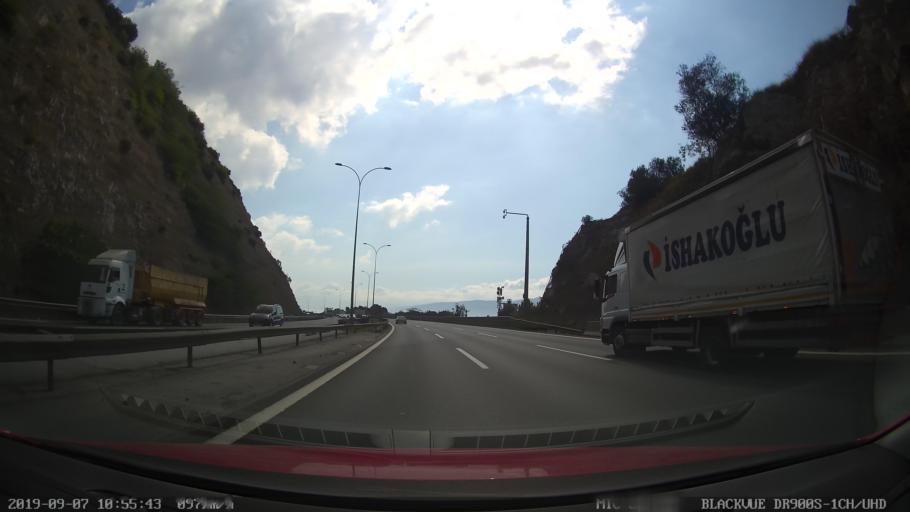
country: TR
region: Kocaeli
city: Hereke
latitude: 40.7781
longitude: 29.6308
